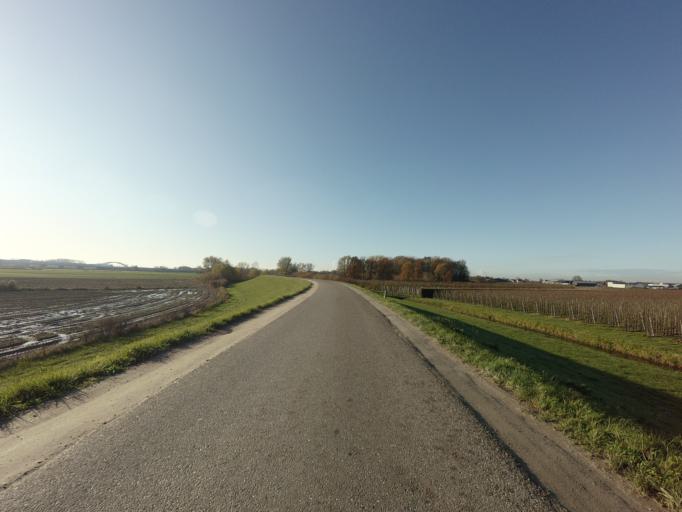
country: NL
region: Gelderland
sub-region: Gemeente Maasdriel
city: Hedel
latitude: 51.7496
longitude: 5.2844
